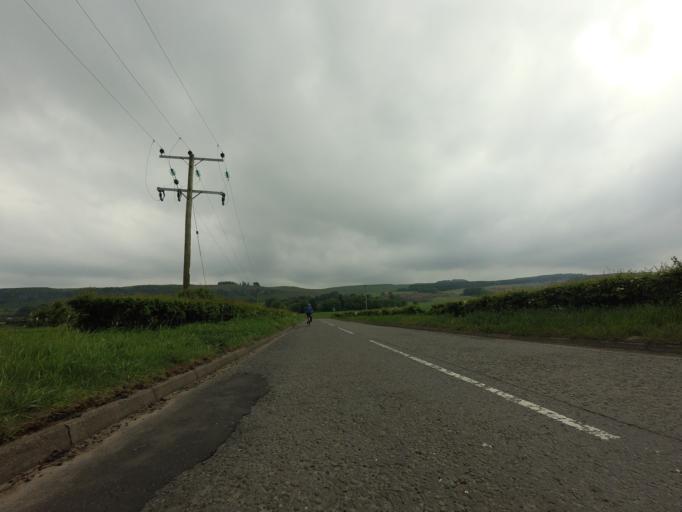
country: GB
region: Scotland
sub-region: Perth and Kinross
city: Kinross
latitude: 56.1678
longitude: -3.4472
